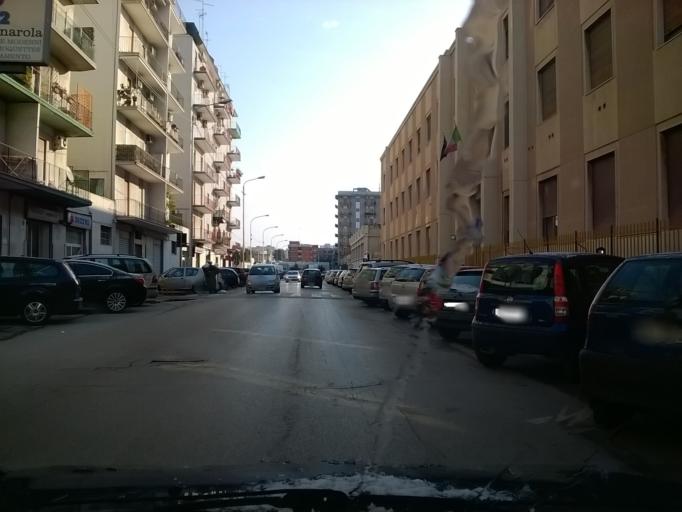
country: IT
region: Apulia
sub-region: Provincia di Taranto
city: Taranto
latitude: 40.4615
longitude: 17.2573
